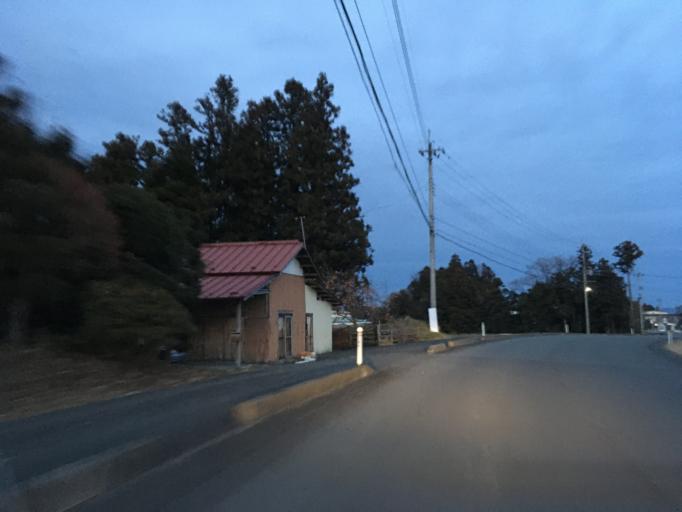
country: JP
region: Miyagi
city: Wakuya
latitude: 38.6976
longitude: 141.1058
